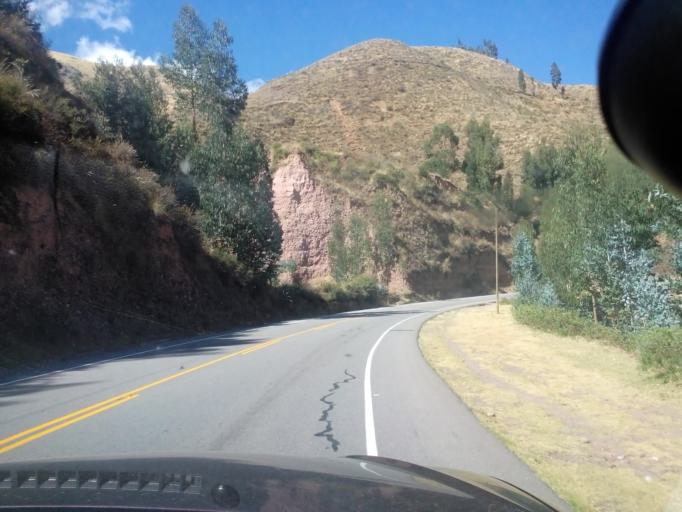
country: PE
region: Cusco
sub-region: Provincia de Quispicanchis
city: Cusipata
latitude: -13.9144
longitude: -71.5015
